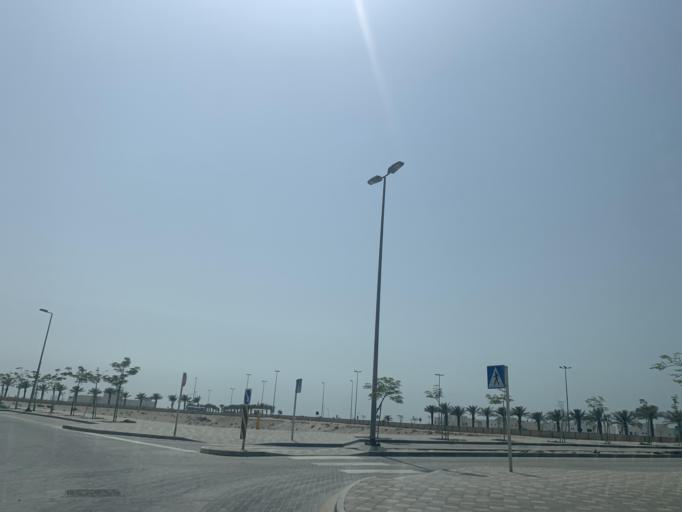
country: BH
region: Muharraq
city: Al Hadd
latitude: 26.2720
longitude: 50.6714
